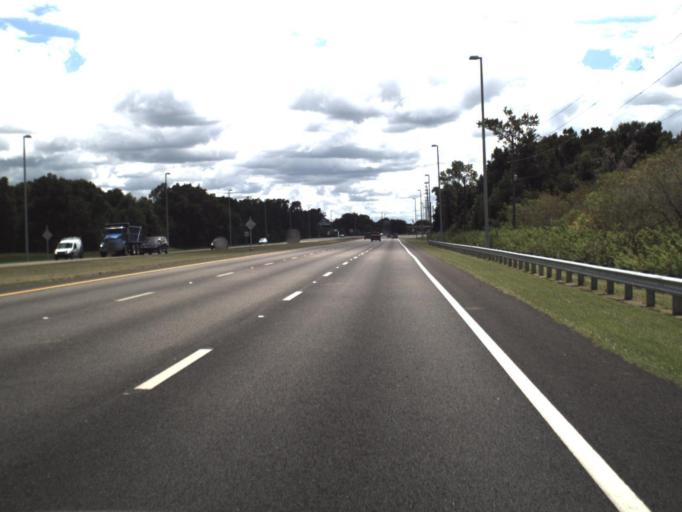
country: US
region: Florida
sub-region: Polk County
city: Bartow
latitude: 27.9172
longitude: -81.8469
